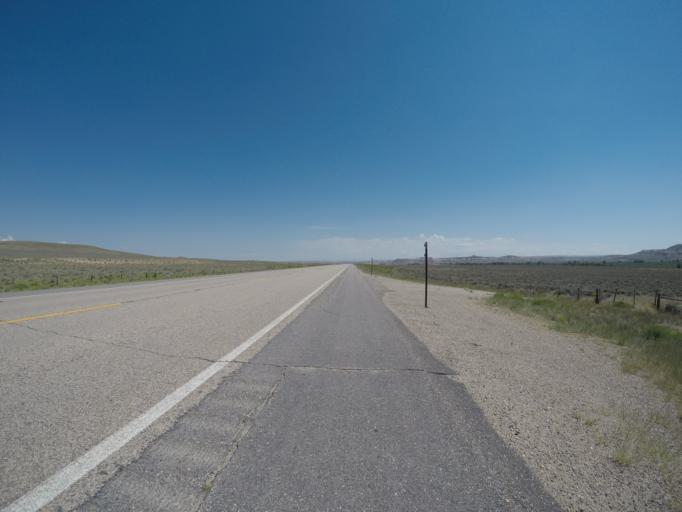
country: US
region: Wyoming
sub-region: Sublette County
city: Marbleton
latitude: 42.4422
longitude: -110.0963
